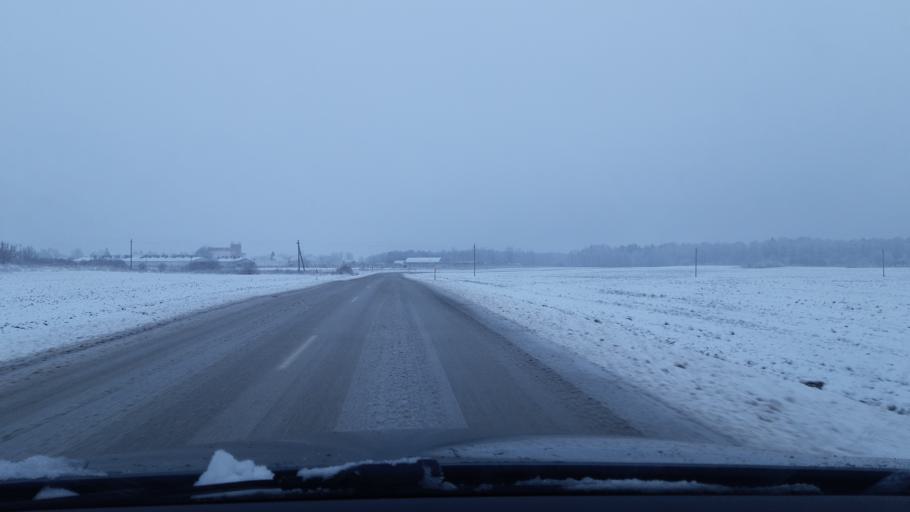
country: LT
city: Kaisiadorys
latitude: 54.8568
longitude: 24.3717
